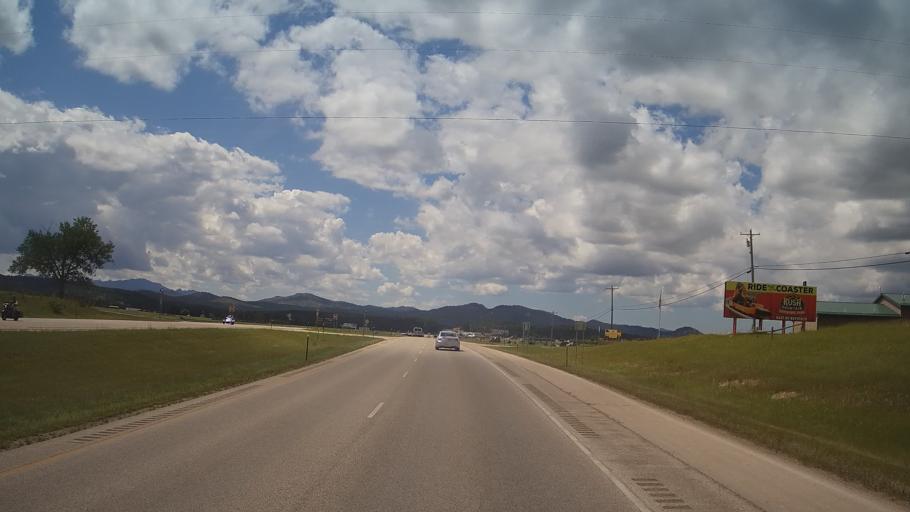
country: US
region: South Dakota
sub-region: Pennington County
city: Colonial Pine Hills
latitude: 43.9732
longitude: -103.3139
